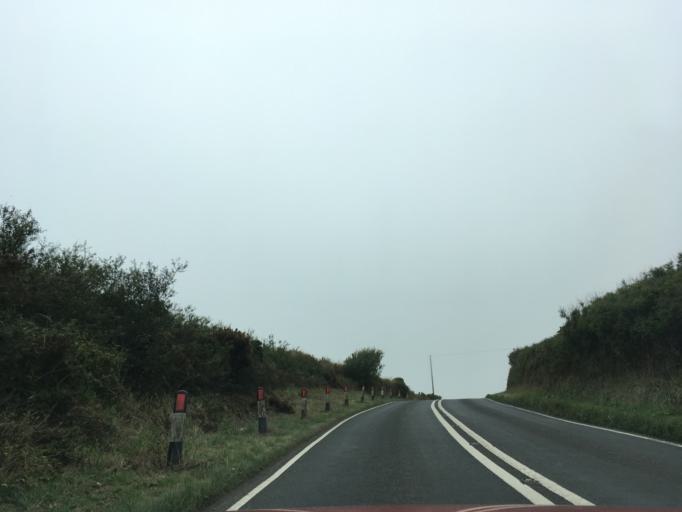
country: GB
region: Wales
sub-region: Pembrokeshire
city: Saint David's
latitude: 51.8798
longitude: -5.2439
